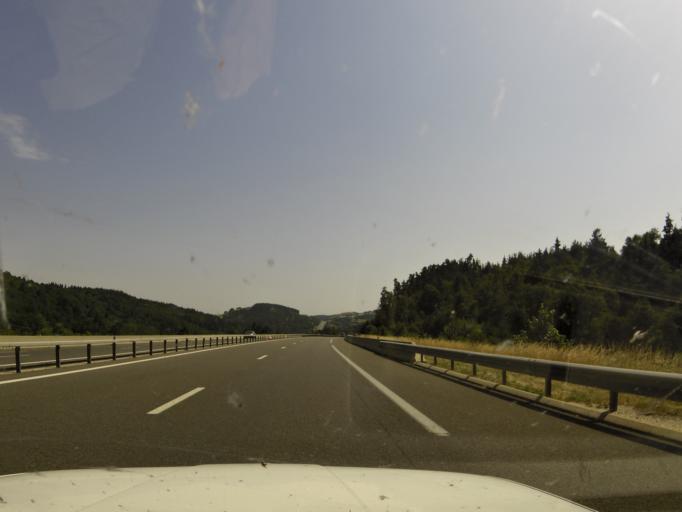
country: FR
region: Languedoc-Roussillon
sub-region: Departement de la Lozere
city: Marvejols
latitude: 44.6078
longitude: 3.2579
